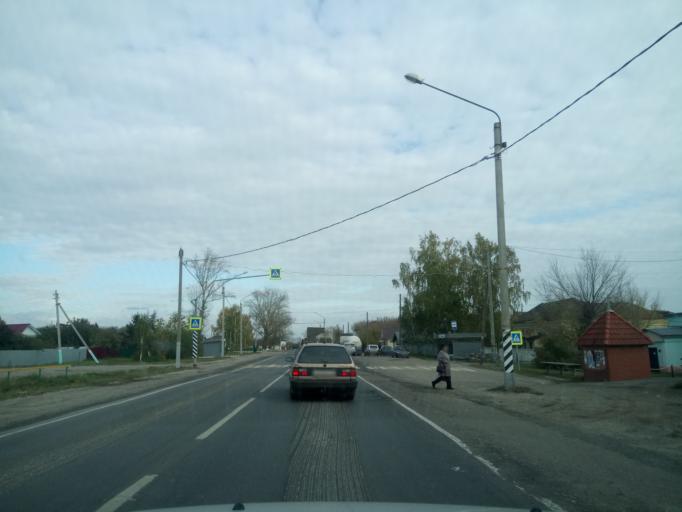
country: RU
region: Nizjnij Novgorod
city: Pochinki
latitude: 54.7934
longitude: 44.9077
